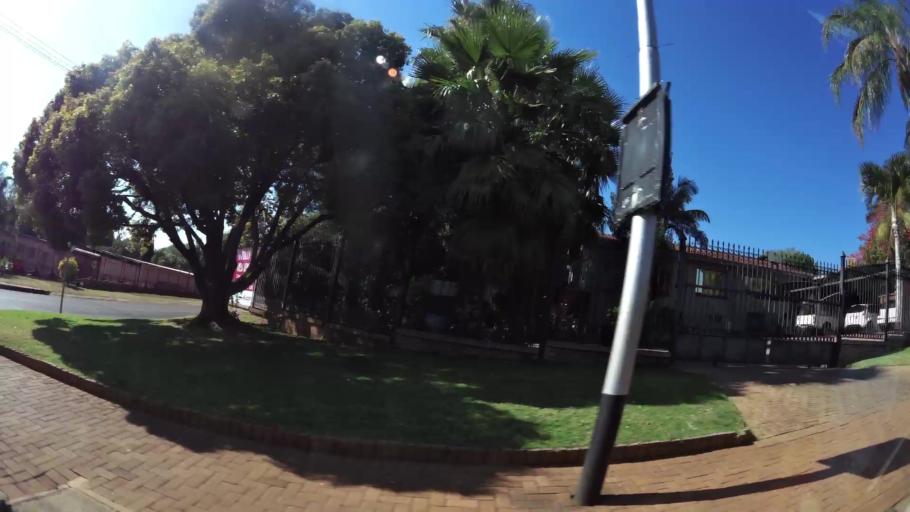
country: ZA
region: Gauteng
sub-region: City of Tshwane Metropolitan Municipality
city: Pretoria
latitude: -25.6826
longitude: 28.2160
